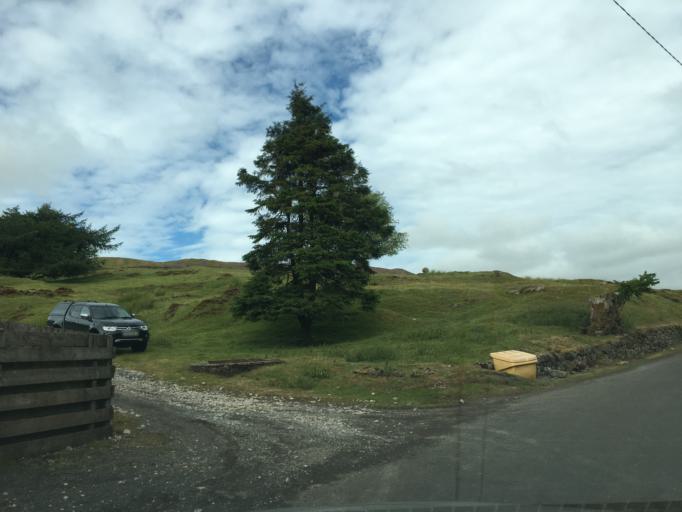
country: GB
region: Scotland
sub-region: Dumfries and Galloway
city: Sanquhar
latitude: 55.3991
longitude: -3.7764
